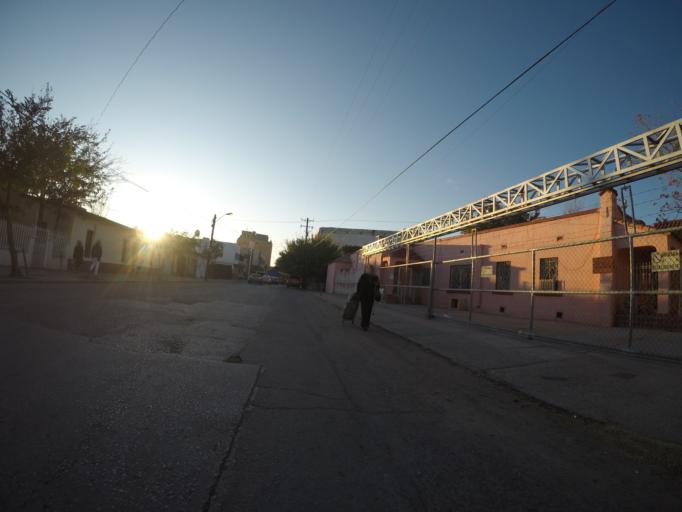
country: MX
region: Chihuahua
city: Ciudad Juarez
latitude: 31.7373
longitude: -106.4794
